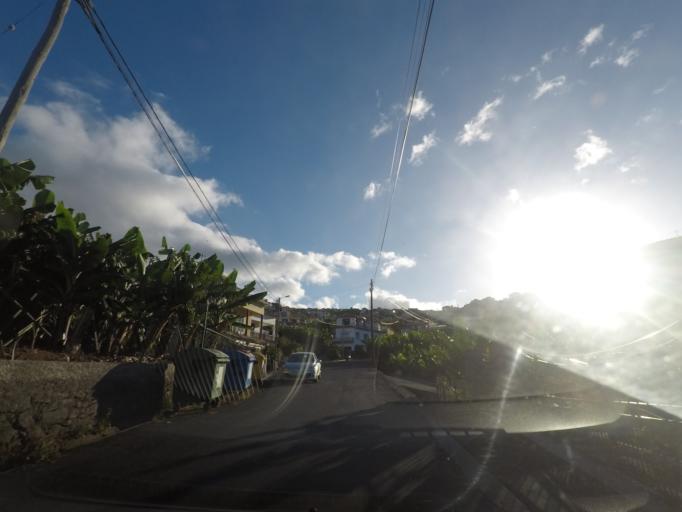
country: PT
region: Madeira
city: Ponta do Sol
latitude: 32.6862
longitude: -17.0949
